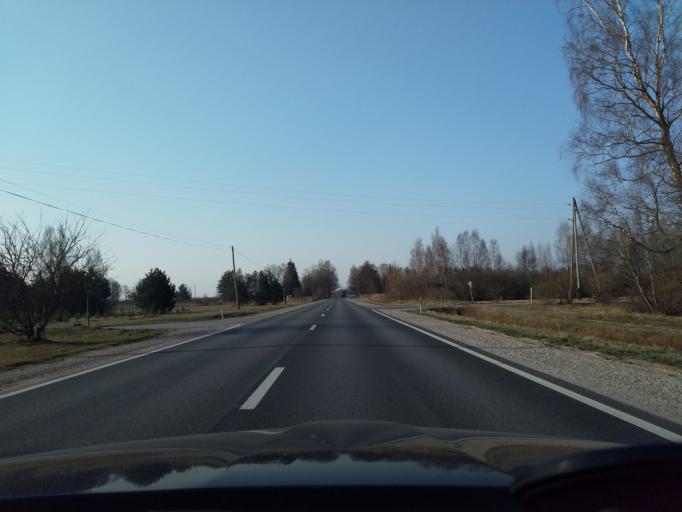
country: LV
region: Nica
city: Nica
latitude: 56.3958
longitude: 21.0038
